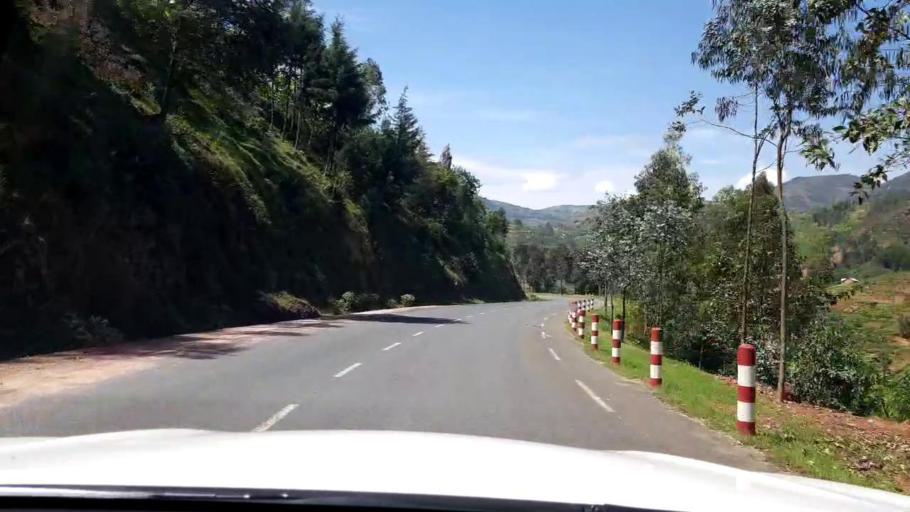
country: RW
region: Southern Province
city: Gitarama
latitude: -1.9144
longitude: 29.6306
